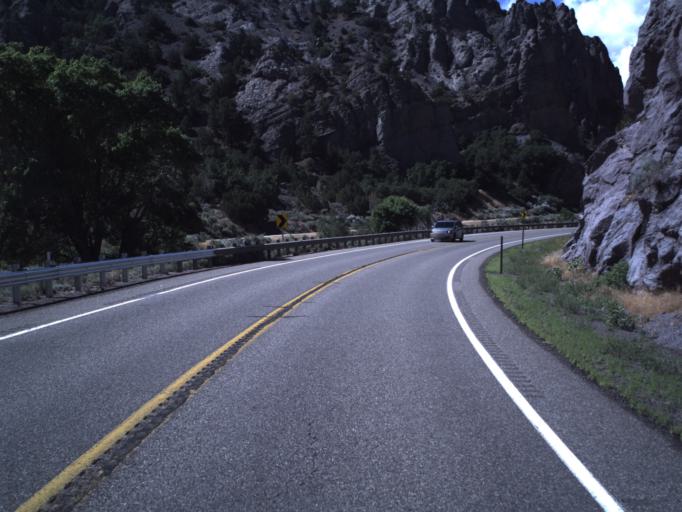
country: US
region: Utah
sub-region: Sevier County
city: Monroe
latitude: 38.5385
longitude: -112.2667
